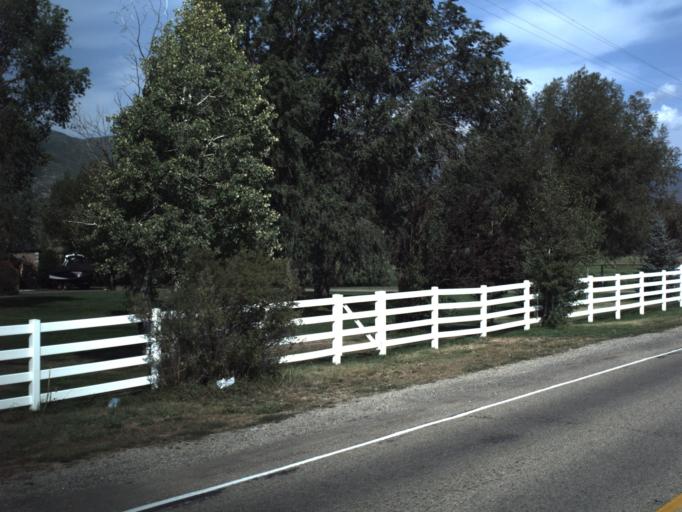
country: US
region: Utah
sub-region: Wasatch County
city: Midway
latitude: 40.4703
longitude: -111.4718
